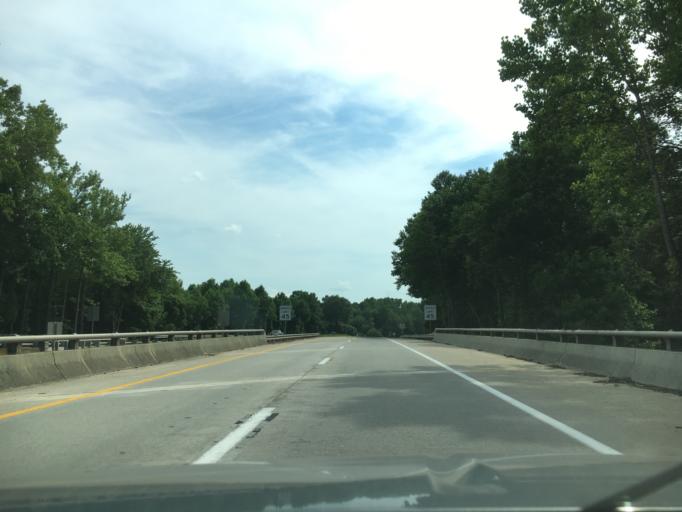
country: US
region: Virginia
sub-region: Prince Edward County
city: Hampden Sydney
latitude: 37.1076
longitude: -78.3556
